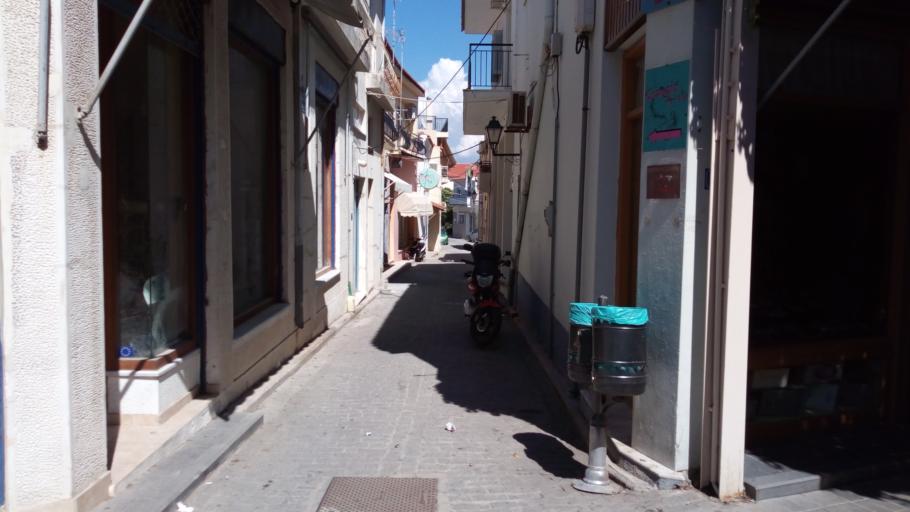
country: GR
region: North Aegean
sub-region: Nomos Lesvou
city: Myrina
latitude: 39.8763
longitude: 25.0595
